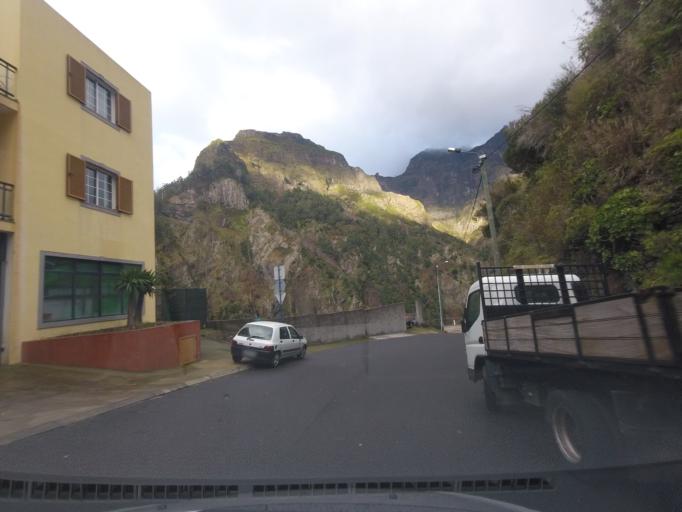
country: PT
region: Madeira
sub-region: Camara de Lobos
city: Curral das Freiras
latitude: 32.7210
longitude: -16.9674
